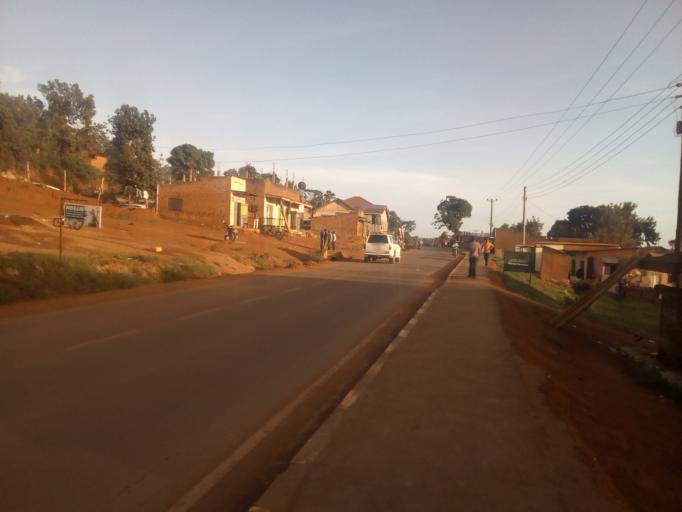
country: UG
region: Central Region
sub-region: Wakiso District
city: Kajansi
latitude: 0.2501
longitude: 32.5706
